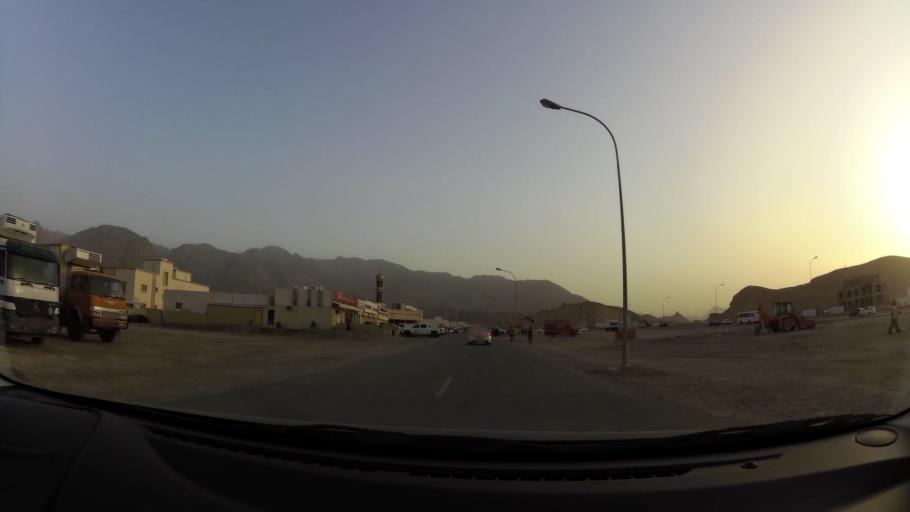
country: OM
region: Muhafazat Masqat
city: Bawshar
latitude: 23.4821
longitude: 58.3103
